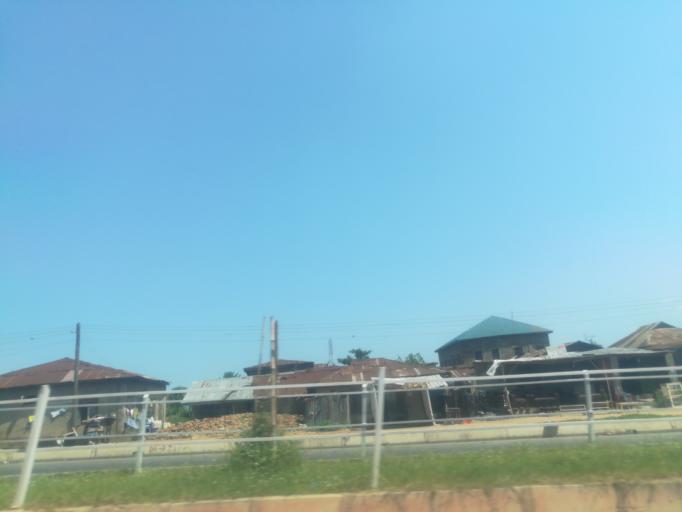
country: NG
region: Ogun
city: Abeokuta
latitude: 7.1671
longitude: 3.3515
